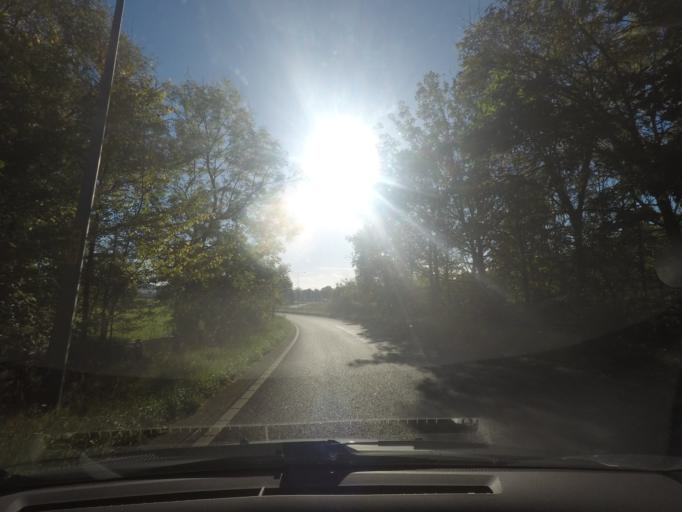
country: GB
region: England
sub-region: East Riding of Yorkshire
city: South Cave
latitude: 53.7619
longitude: -0.5979
